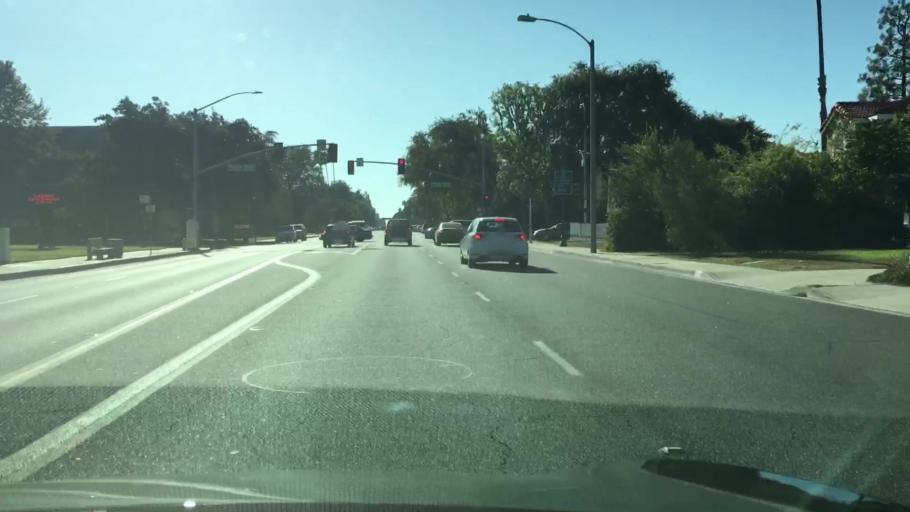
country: US
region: California
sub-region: Los Angeles County
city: Arcadia
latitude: 34.1275
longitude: -118.0452
